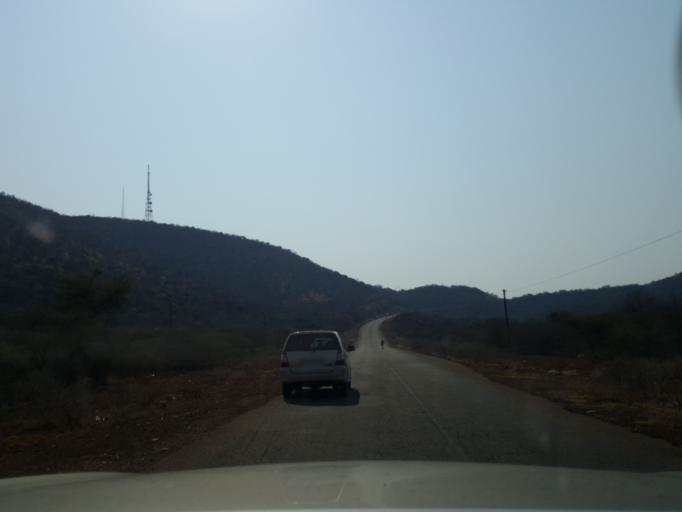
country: BW
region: South East
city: Lobatse
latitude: -25.2846
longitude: 25.8625
